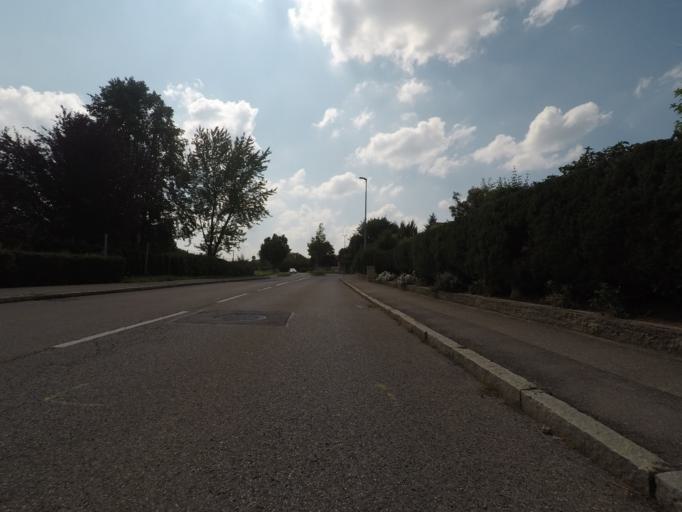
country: DE
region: Baden-Wuerttemberg
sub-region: Regierungsbezirk Stuttgart
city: Weinstadt-Endersbach
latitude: 48.7766
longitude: 9.3909
